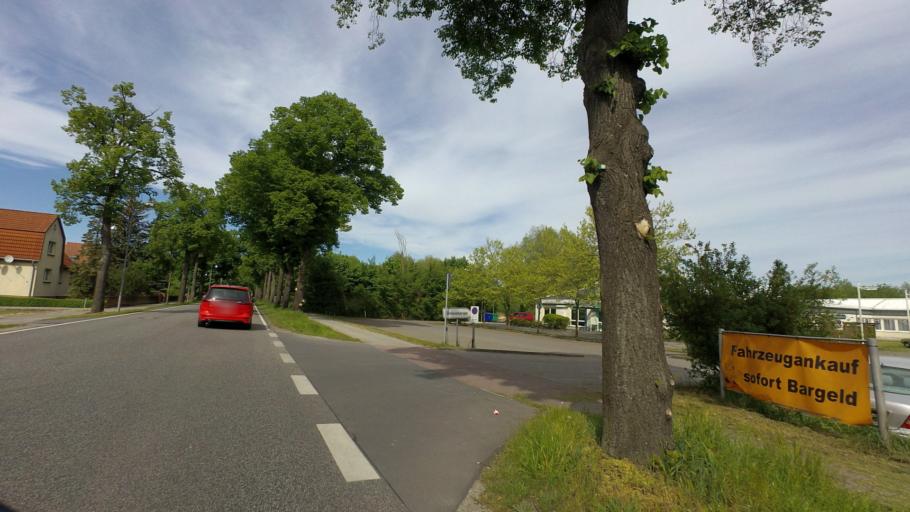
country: DE
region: Brandenburg
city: Zossen
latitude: 52.2280
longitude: 13.4441
